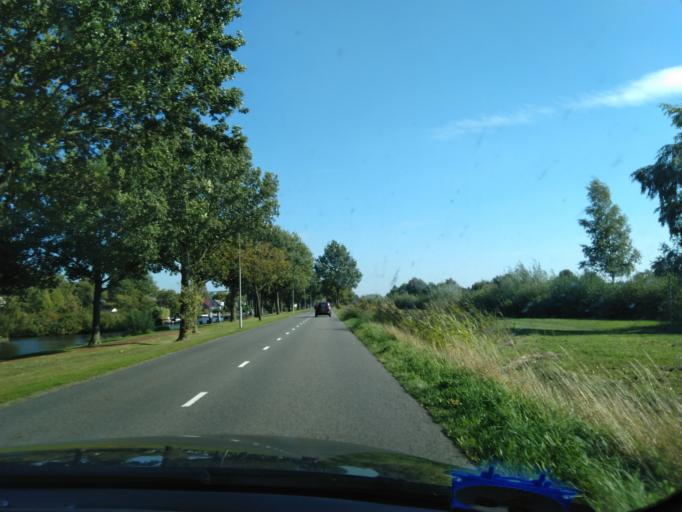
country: NL
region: Groningen
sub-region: Gemeente Veendam
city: Veendam
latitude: 53.0901
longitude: 6.8467
